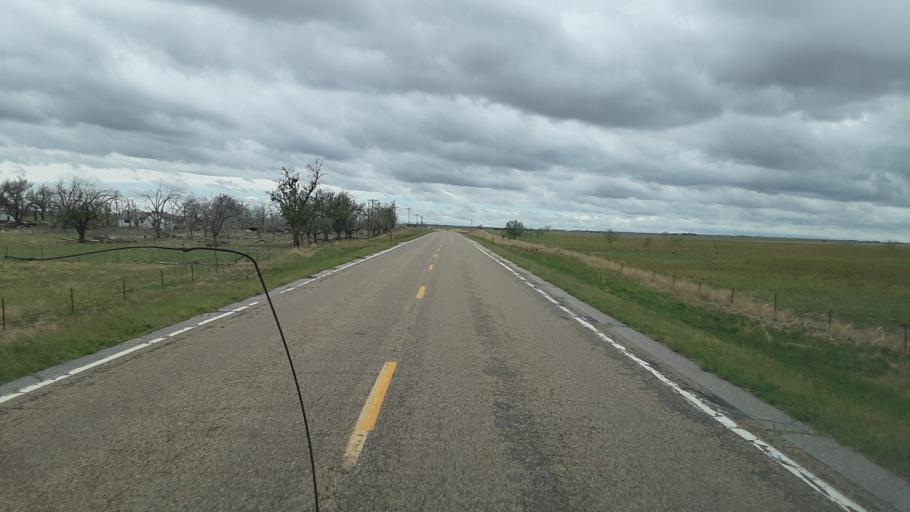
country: US
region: Colorado
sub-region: El Paso County
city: Ellicott
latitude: 38.8398
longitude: -103.9381
